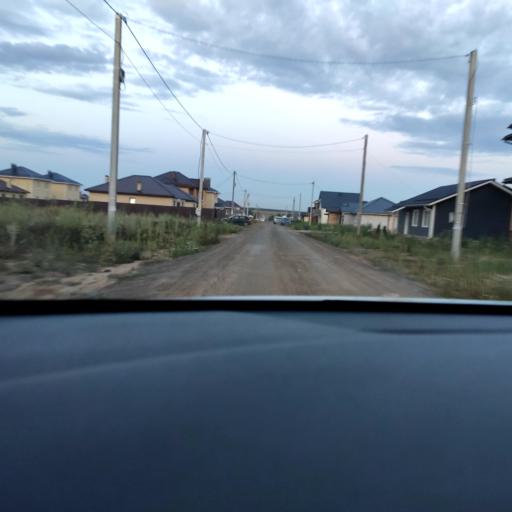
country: RU
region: Tatarstan
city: Stolbishchi
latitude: 55.7161
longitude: 49.3008
